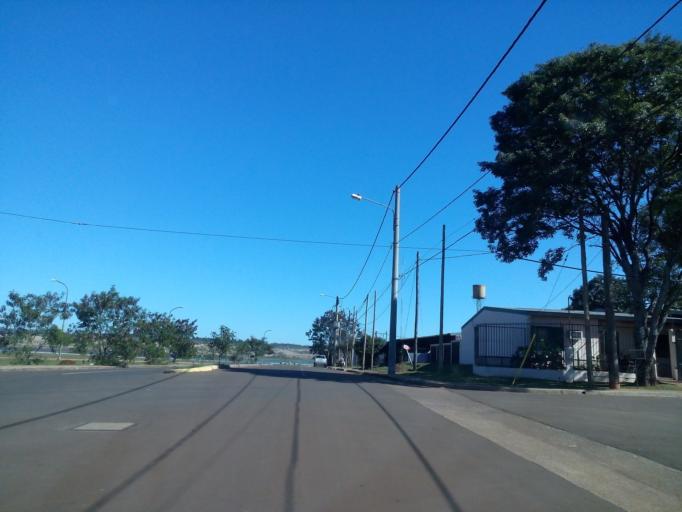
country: AR
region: Misiones
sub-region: Departamento de Capital
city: Posadas
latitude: -27.3857
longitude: -55.9492
